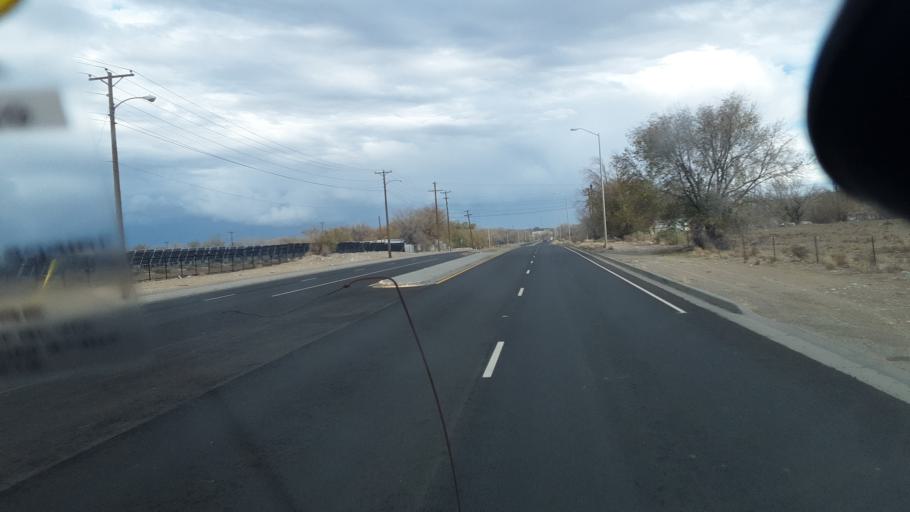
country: US
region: New Mexico
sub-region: San Juan County
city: Farmington
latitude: 36.7192
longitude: -108.2153
